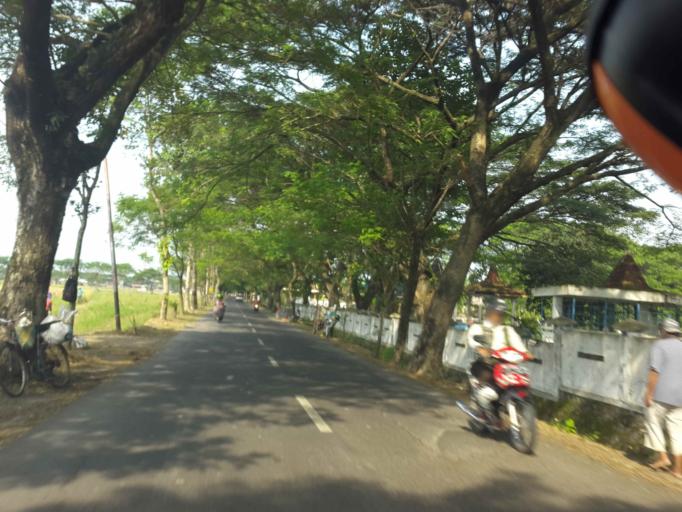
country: ID
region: Central Java
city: Sragen
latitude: -7.4201
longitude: 111.0126
